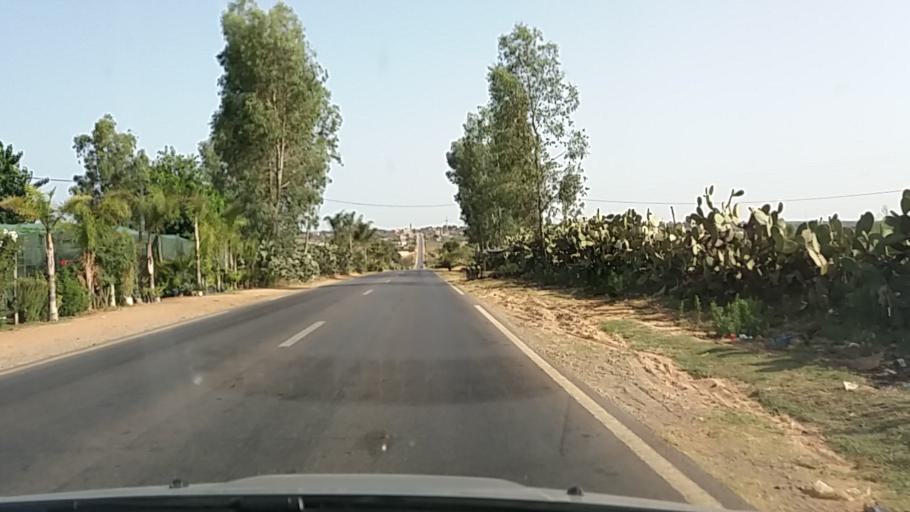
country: MA
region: Gharb-Chrarda-Beni Hssen
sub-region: Kenitra Province
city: Kenitra
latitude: 34.1111
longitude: -6.5591
